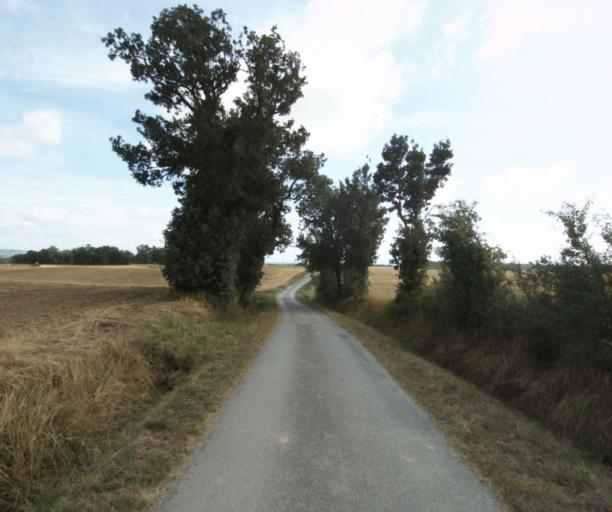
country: FR
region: Midi-Pyrenees
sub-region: Departement du Tarn
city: Soreze
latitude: 43.4781
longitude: 2.0883
